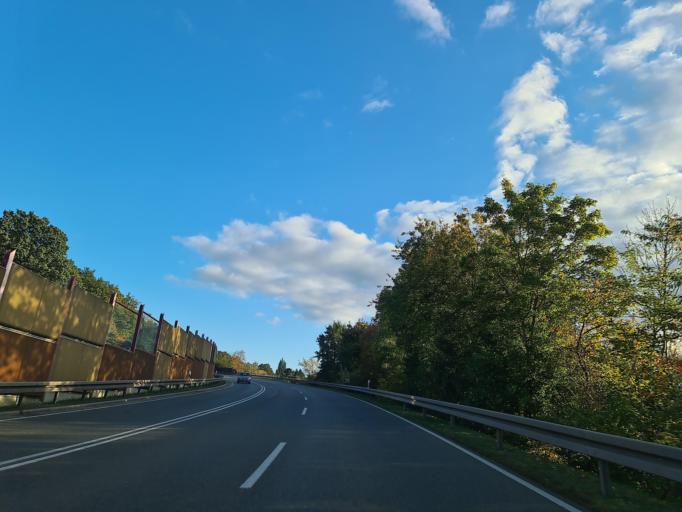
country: DE
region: Thuringia
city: Weida
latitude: 50.7746
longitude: 12.0680
